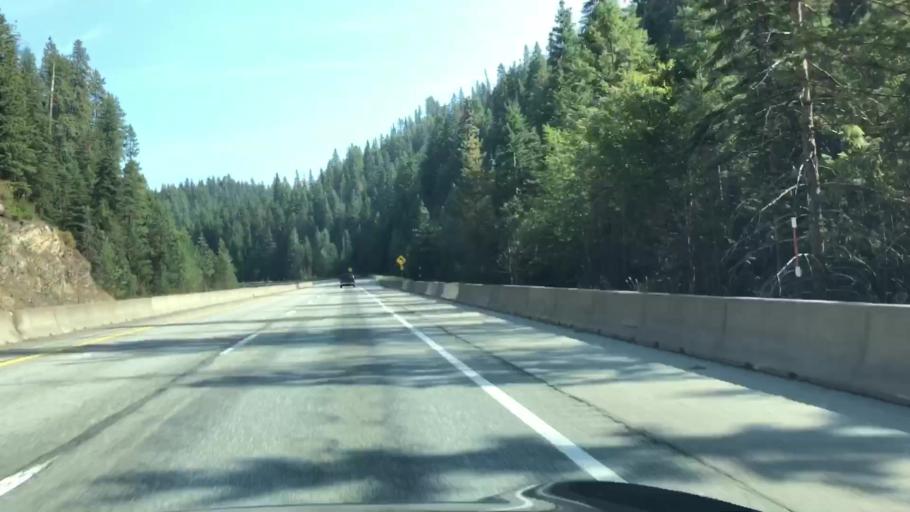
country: US
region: Idaho
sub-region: Kootenai County
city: Coeur d'Alene
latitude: 47.6233
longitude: -116.5839
